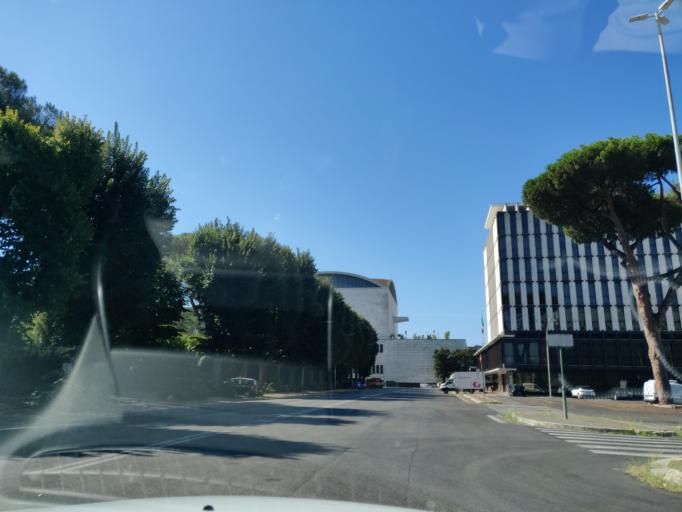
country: IT
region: Latium
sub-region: Citta metropolitana di Roma Capitale
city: Rome
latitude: 41.8359
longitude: 12.4750
